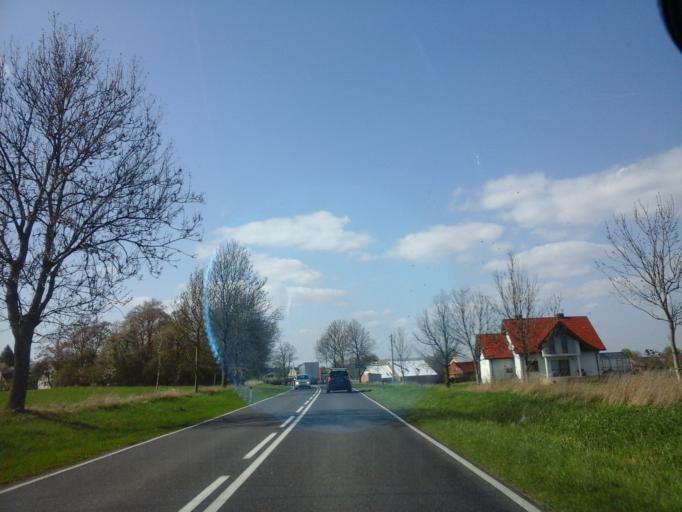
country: PL
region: West Pomeranian Voivodeship
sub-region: Powiat stargardzki
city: Suchan
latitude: 53.2218
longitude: 15.3028
